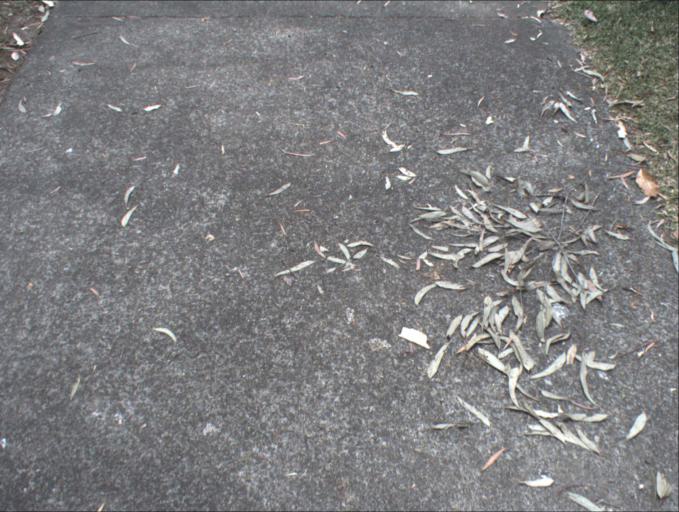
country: AU
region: Queensland
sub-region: Logan
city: Slacks Creek
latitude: -27.6528
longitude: 153.1907
